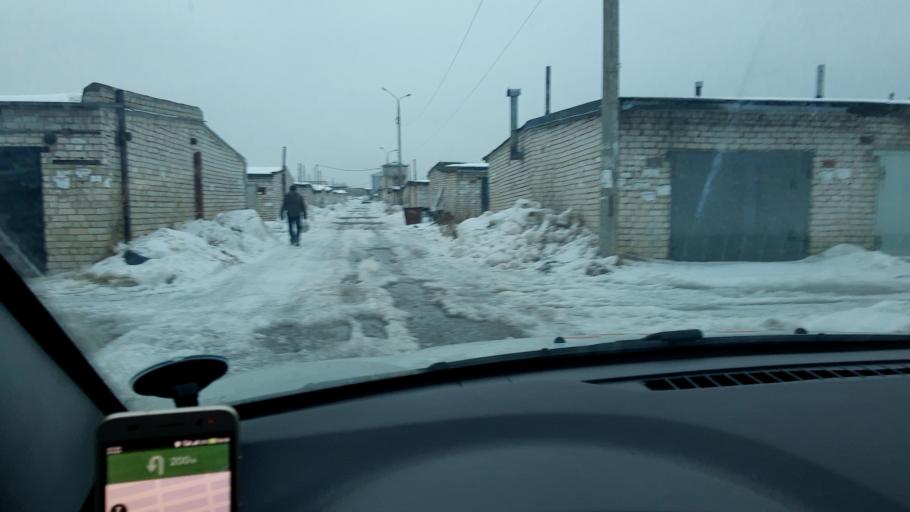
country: RU
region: Nizjnij Novgorod
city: Gorbatovka
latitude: 56.2525
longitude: 43.8315
